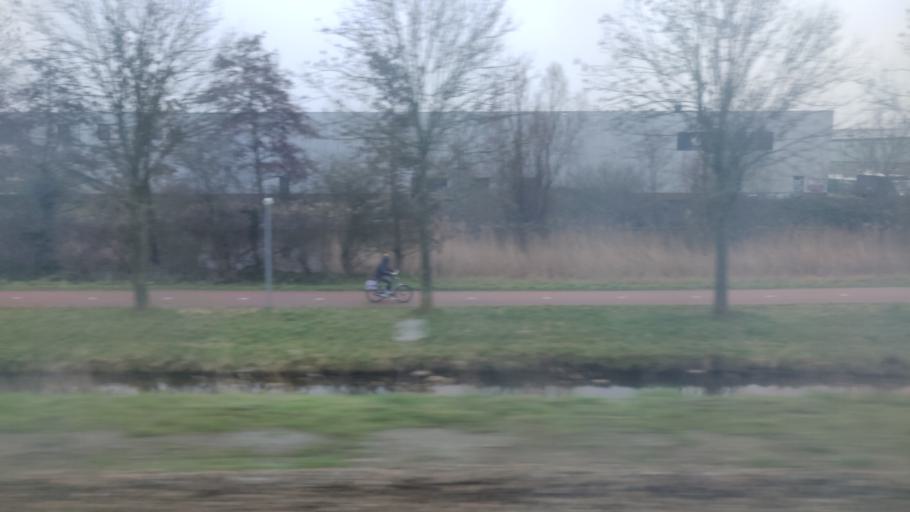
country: NL
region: North Holland
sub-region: Gemeente Langedijk
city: Broek op Langedijk
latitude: 52.6586
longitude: 4.7974
